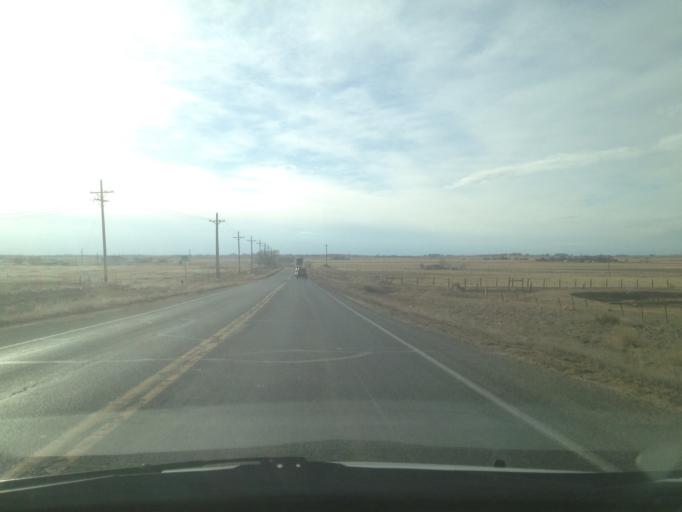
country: US
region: Colorado
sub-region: Weld County
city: Hudson
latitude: 40.0805
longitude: -104.6580
